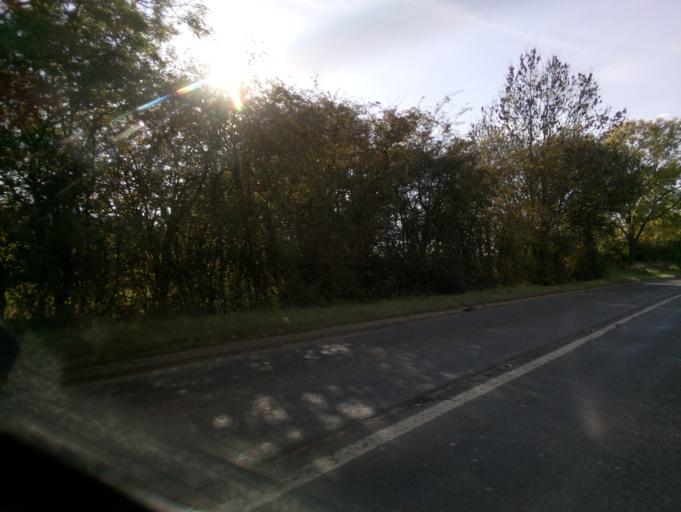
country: GB
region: England
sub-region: Herefordshire
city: Kinnersley
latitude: 52.1201
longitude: -2.9926
